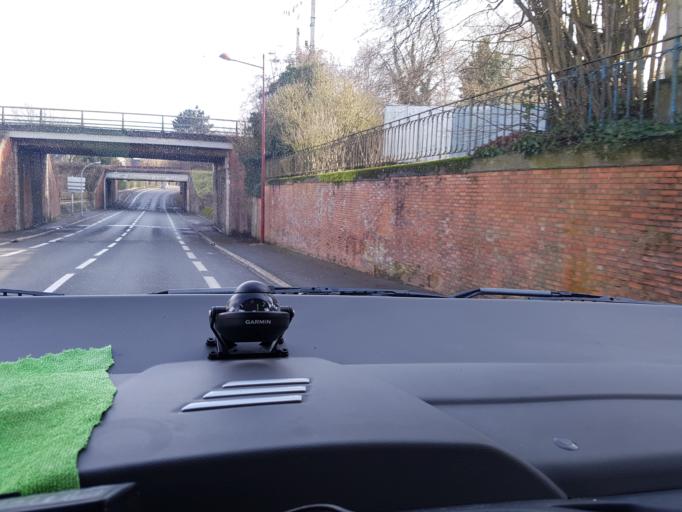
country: FR
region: Picardie
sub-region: Departement de l'Aisne
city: Hirson
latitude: 49.9169
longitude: 4.0870
